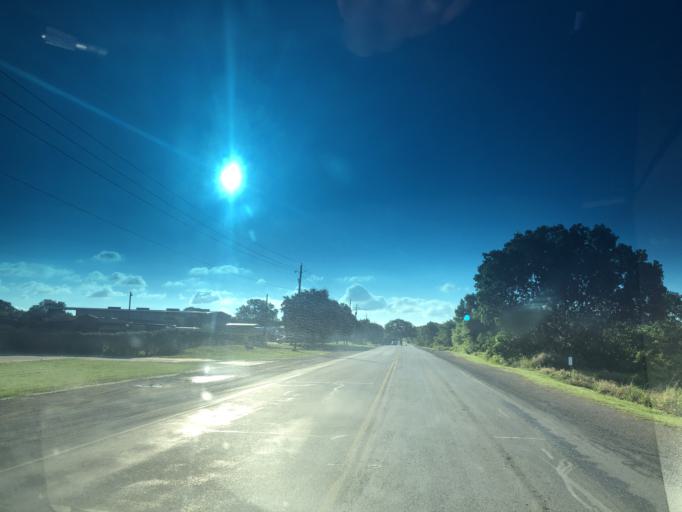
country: US
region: Texas
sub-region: Dallas County
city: Grand Prairie
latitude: 32.7779
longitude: -97.0106
